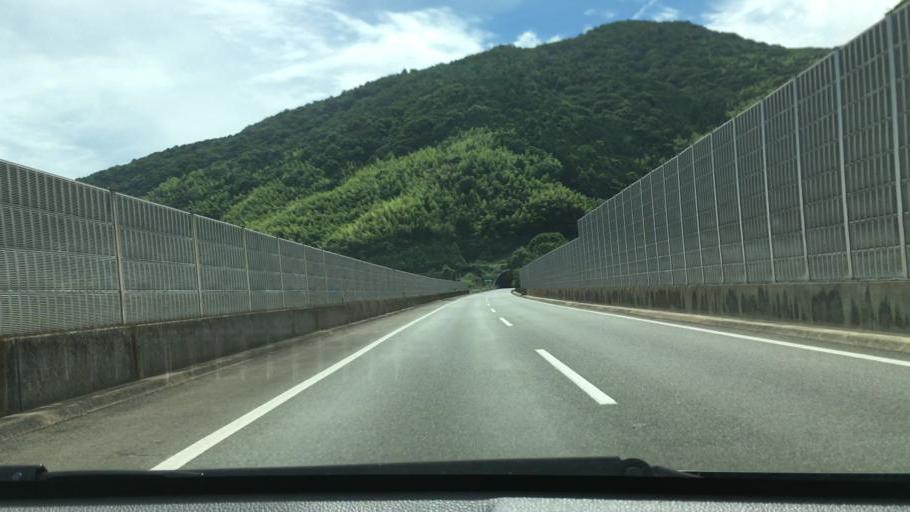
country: JP
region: Yamaguchi
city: Hofu
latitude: 34.0550
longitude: 131.6400
